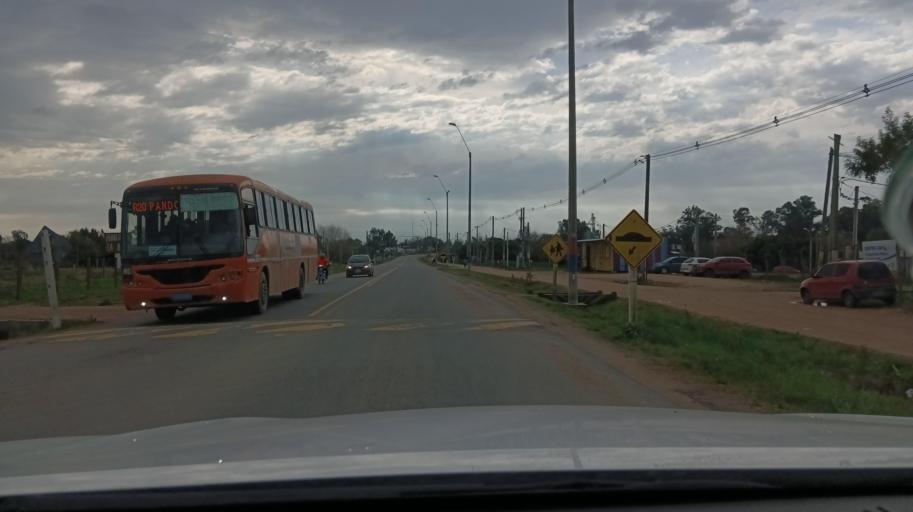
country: UY
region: Canelones
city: Toledo
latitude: -34.7391
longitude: -56.1129
